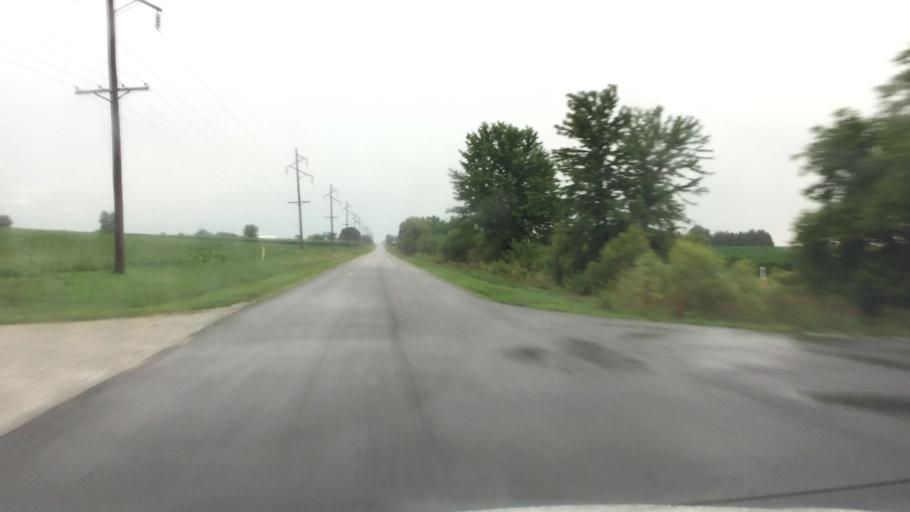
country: US
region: Illinois
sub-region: Hancock County
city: Hamilton
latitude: 40.4397
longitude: -91.2712
